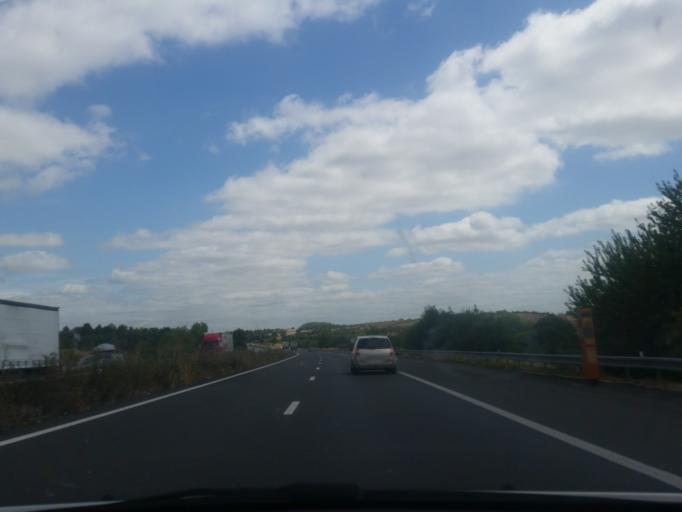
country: FR
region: Pays de la Loire
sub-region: Departement de Maine-et-Loire
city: Ingrandes
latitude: 47.4209
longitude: -0.9512
